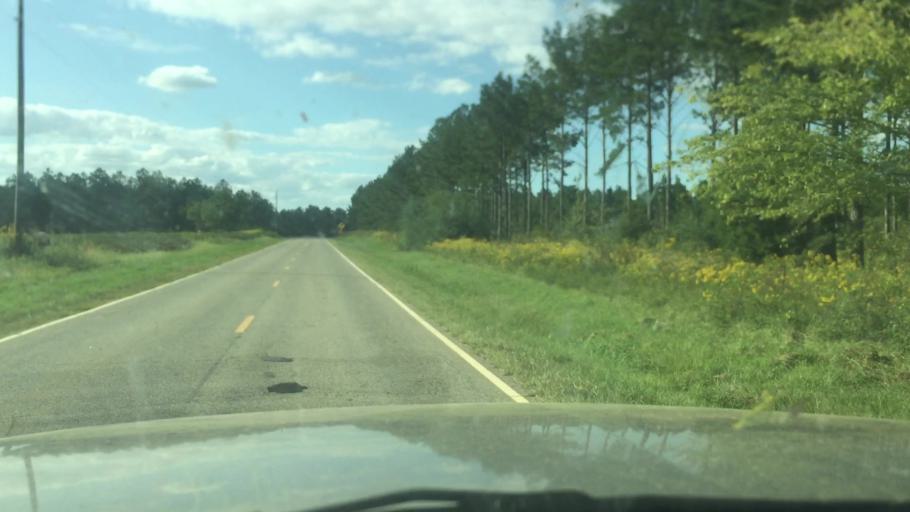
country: US
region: Georgia
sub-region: Terrell County
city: Dawson
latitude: 31.7406
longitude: -84.3475
